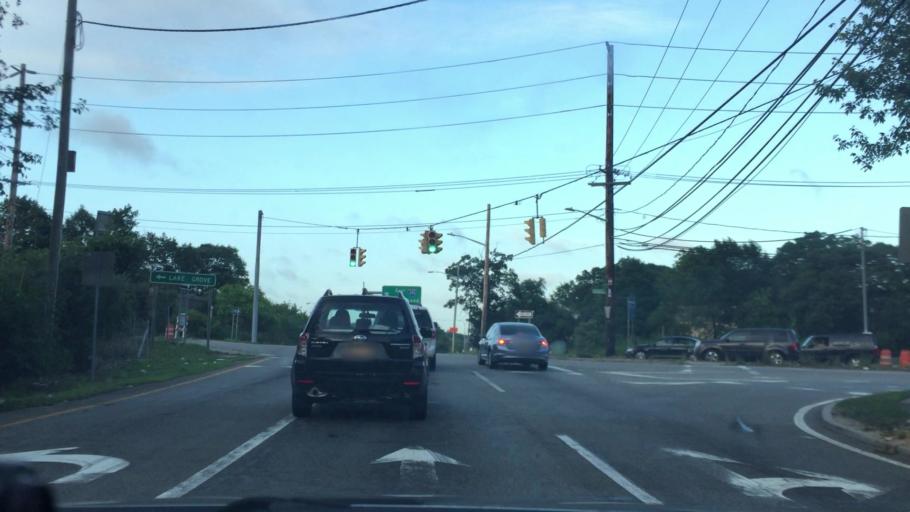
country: US
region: New York
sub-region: Suffolk County
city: Ronkonkoma
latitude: 40.8127
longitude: -73.1086
